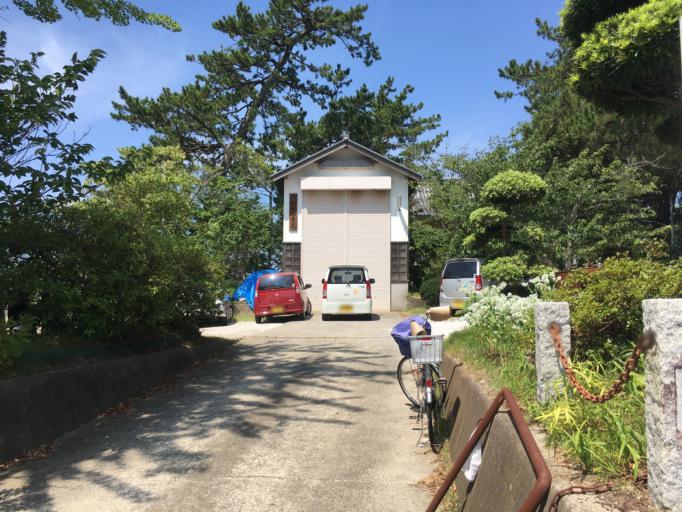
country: JP
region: Chiba
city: Tateyama
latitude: 34.9962
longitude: 139.8669
